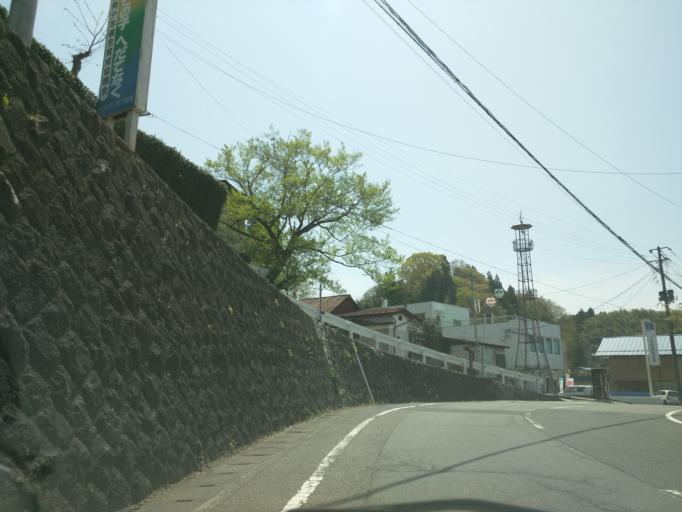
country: JP
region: Fukushima
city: Nihommatsu
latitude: 37.5618
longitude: 140.5088
